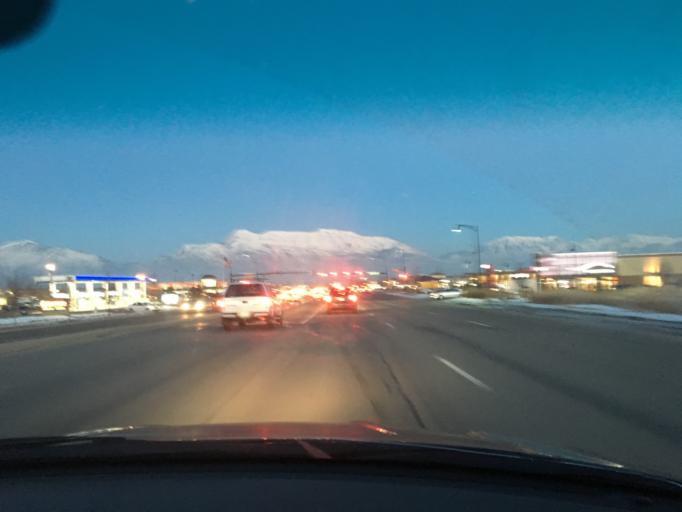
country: US
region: Utah
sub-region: Utah County
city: Saratoga Springs
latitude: 40.3875
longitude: -111.9187
